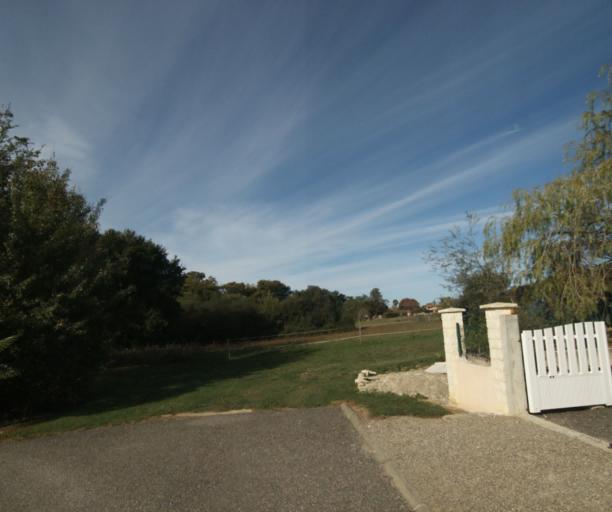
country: FR
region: Midi-Pyrenees
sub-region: Departement du Gers
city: Eauze
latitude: 43.8843
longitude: 0.1373
